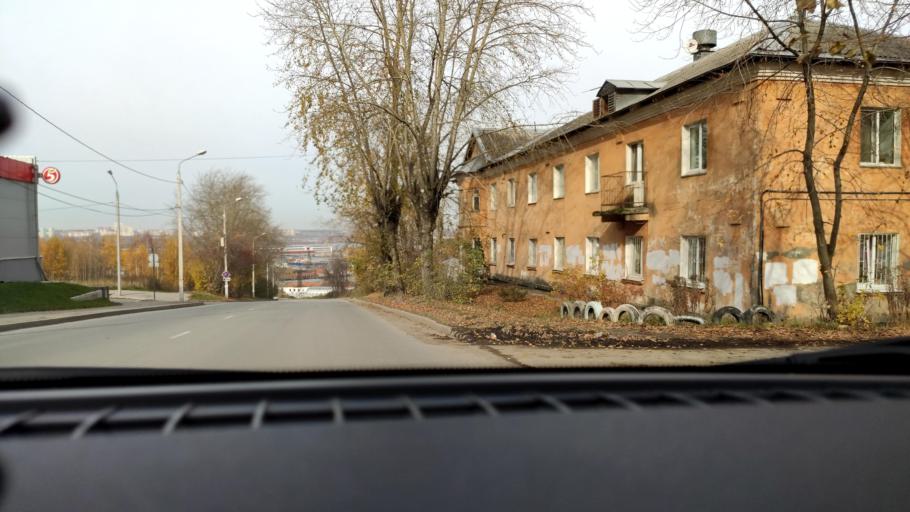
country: RU
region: Perm
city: Perm
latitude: 58.0684
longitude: 56.3552
